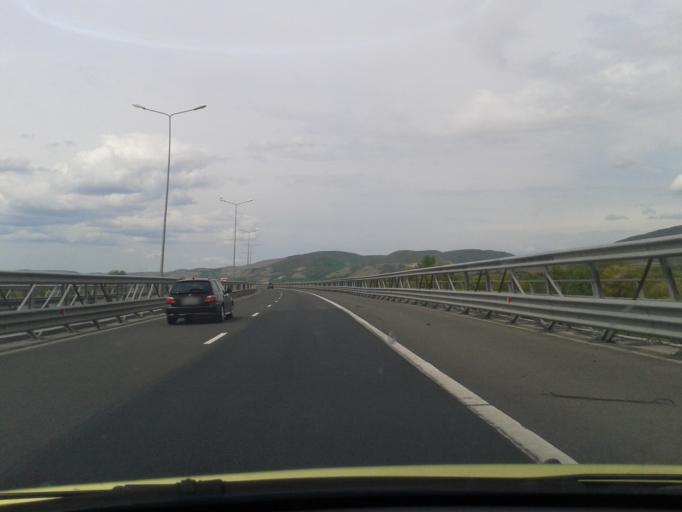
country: RO
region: Hunedoara
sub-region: Oras Simeria
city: Simeria
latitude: 45.8640
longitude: 23.0256
